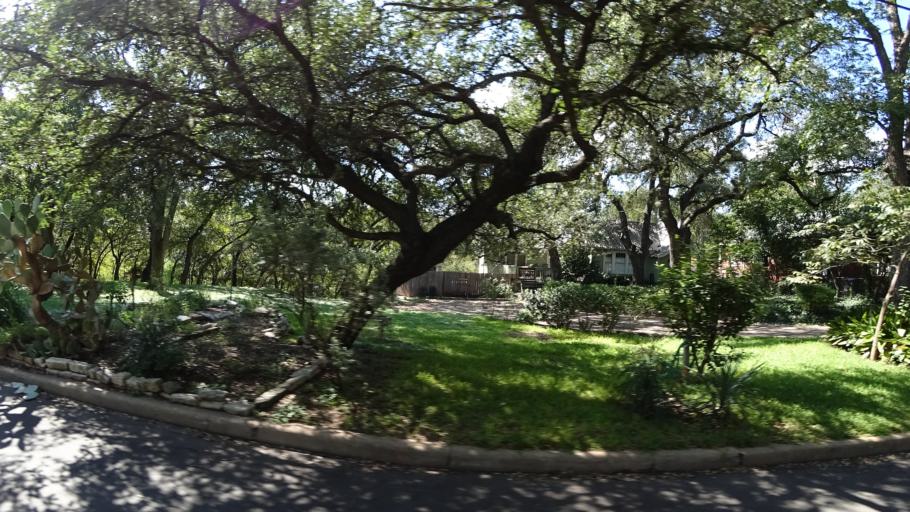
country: US
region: Texas
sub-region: Travis County
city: Austin
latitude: 30.2959
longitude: -97.7481
